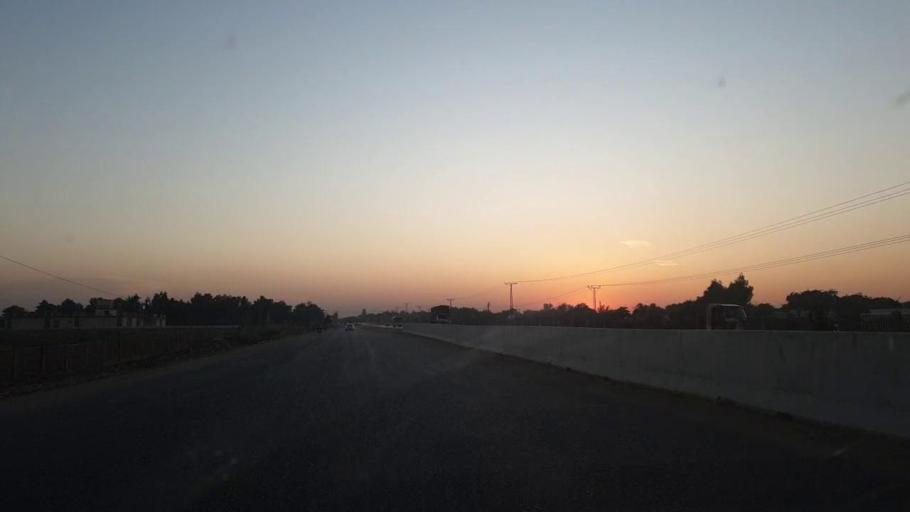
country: PK
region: Sindh
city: Jamshoro
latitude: 25.4189
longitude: 68.2782
